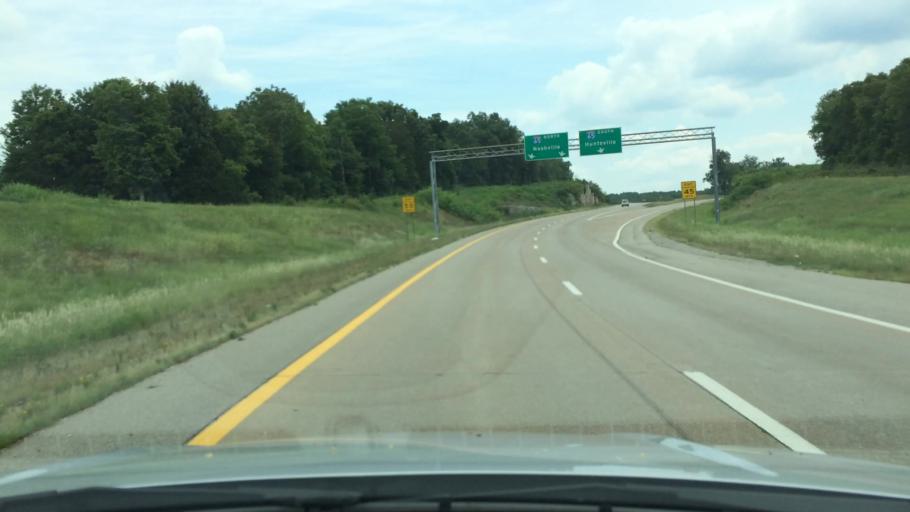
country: US
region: Tennessee
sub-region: Maury County
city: Spring Hill
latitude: 35.7392
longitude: -86.8797
